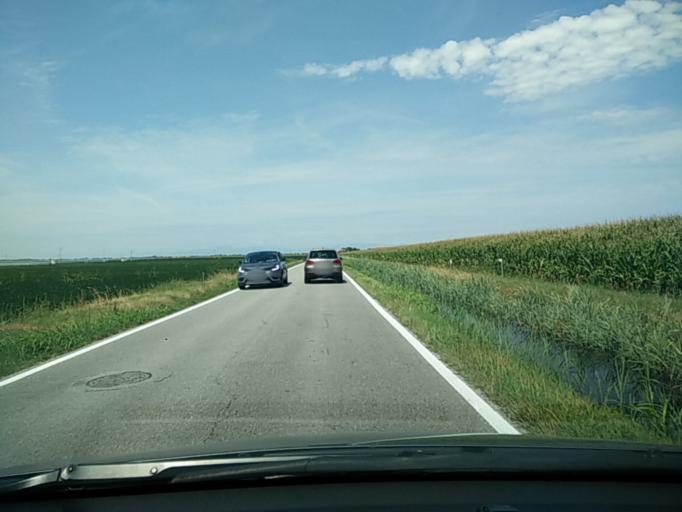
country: IT
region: Veneto
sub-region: Provincia di Venezia
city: Iesolo
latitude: 45.5621
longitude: 12.6375
